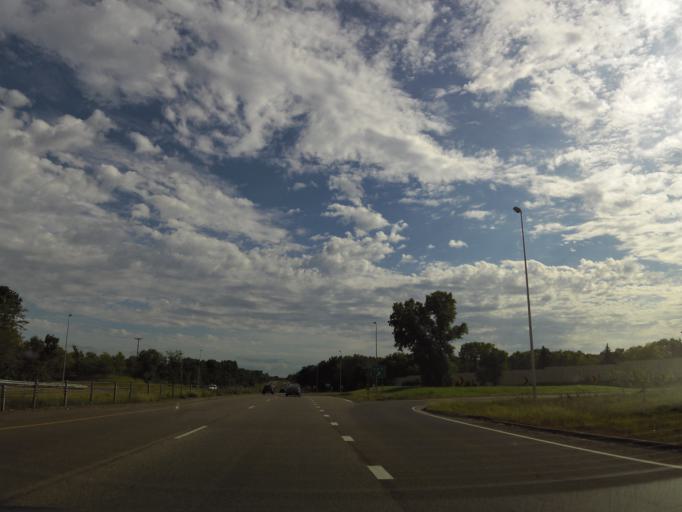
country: US
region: Minnesota
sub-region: Hennepin County
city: Osseo
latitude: 45.0828
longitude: -93.4023
